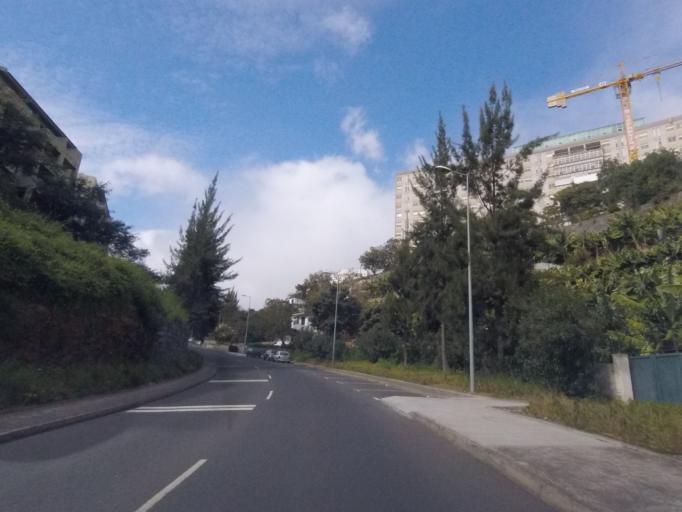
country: PT
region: Madeira
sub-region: Funchal
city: Funchal
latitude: 32.6474
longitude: -16.9247
